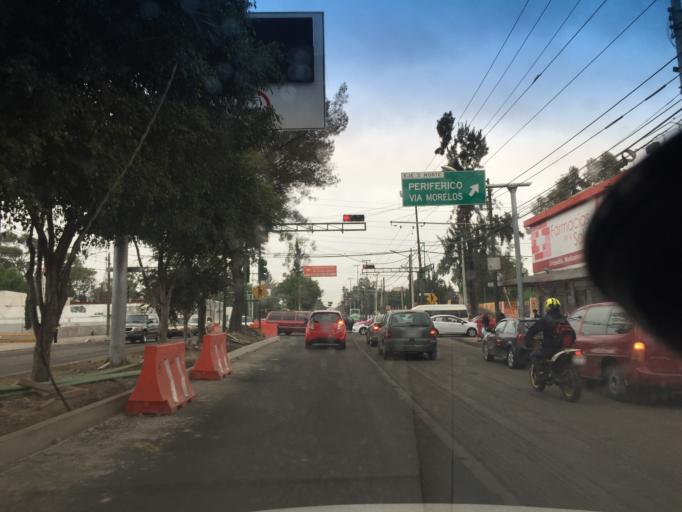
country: MX
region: Mexico City
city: Gustavo A. Madero
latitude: 19.4760
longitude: -99.0902
